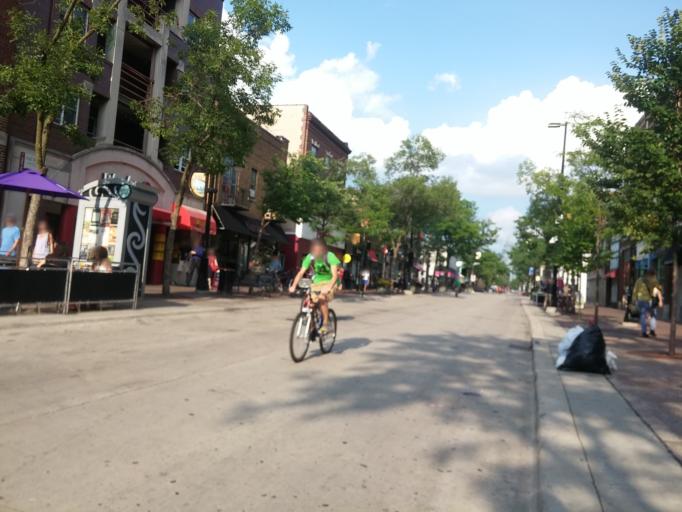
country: US
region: Wisconsin
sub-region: Dane County
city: Madison
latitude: 43.0749
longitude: -89.3945
